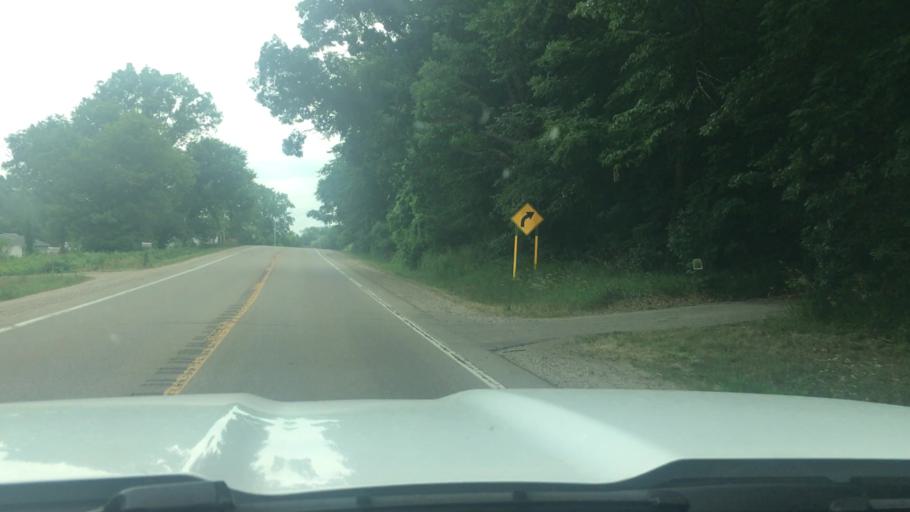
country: US
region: Michigan
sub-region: Ionia County
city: Saranac
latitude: 42.9345
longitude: -85.2675
